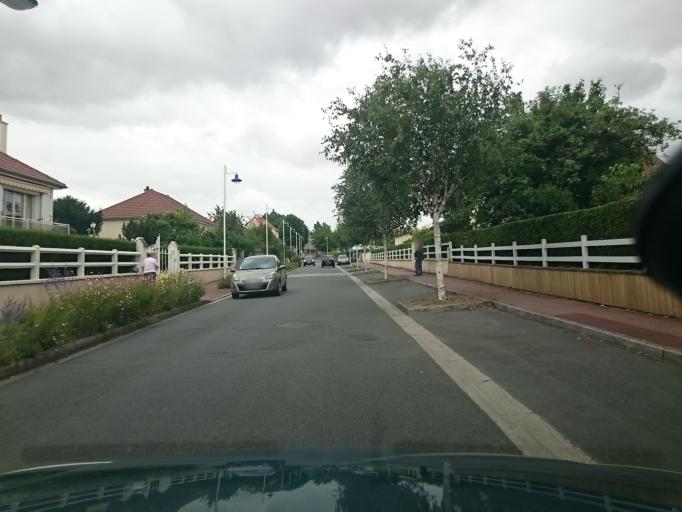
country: FR
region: Lower Normandy
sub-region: Departement du Calvados
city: Ifs
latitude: 49.1410
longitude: -0.3515
